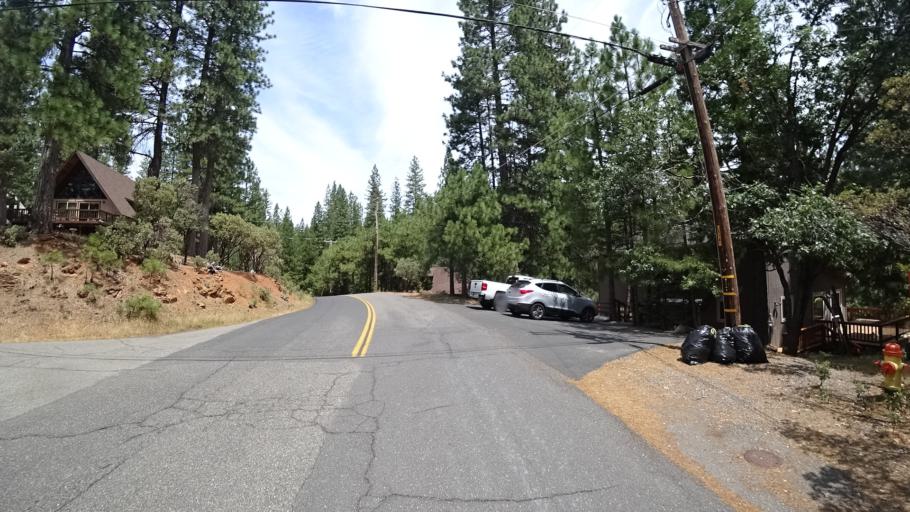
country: US
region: California
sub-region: Calaveras County
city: Arnold
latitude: 38.2431
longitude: -120.3512
